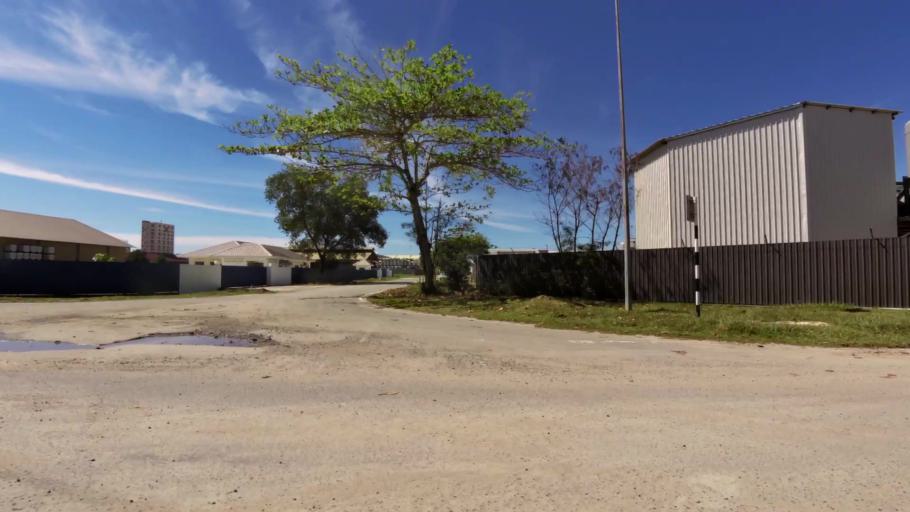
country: BN
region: Brunei and Muara
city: Bandar Seri Begawan
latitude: 5.0144
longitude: 115.0621
